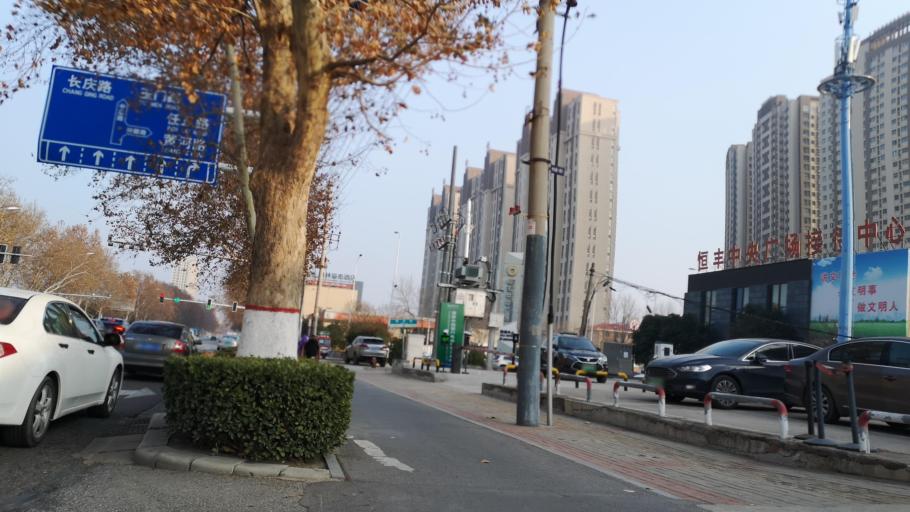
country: CN
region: Henan Sheng
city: Zhongyuanlu
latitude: 35.7790
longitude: 115.0539
